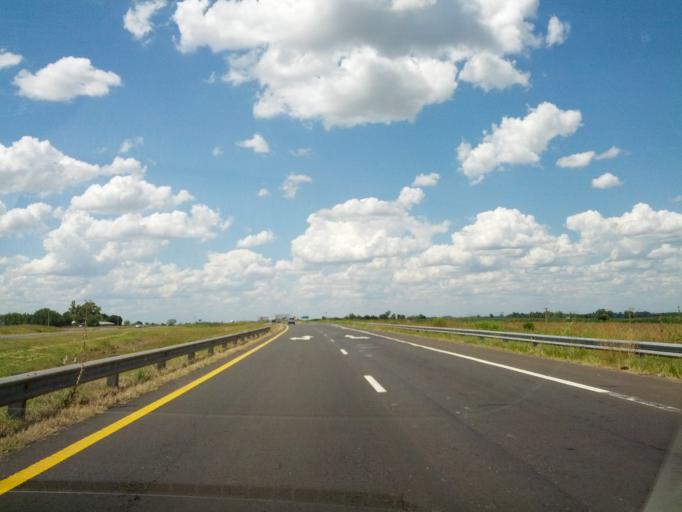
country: AR
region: Entre Rios
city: Colonia Elia
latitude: -32.5821
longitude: -58.3920
